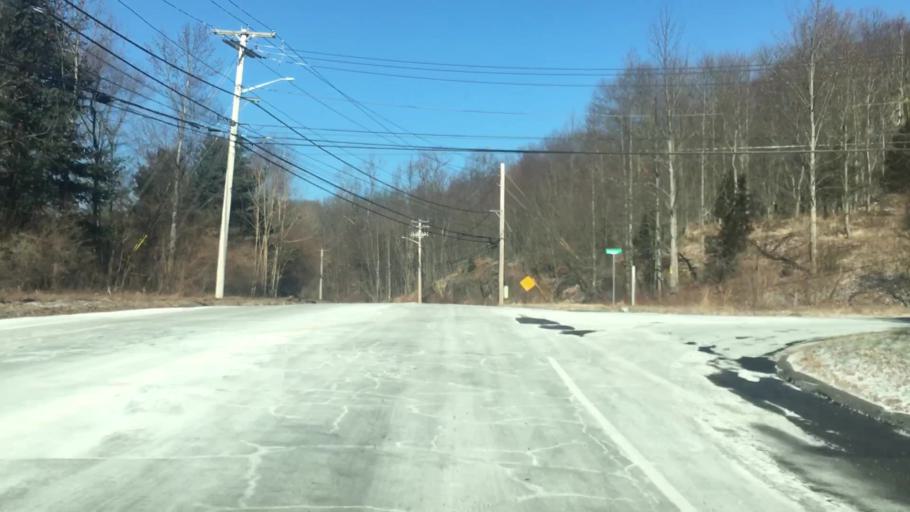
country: US
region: Connecticut
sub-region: Fairfield County
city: Shelton
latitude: 41.2918
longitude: -73.0841
